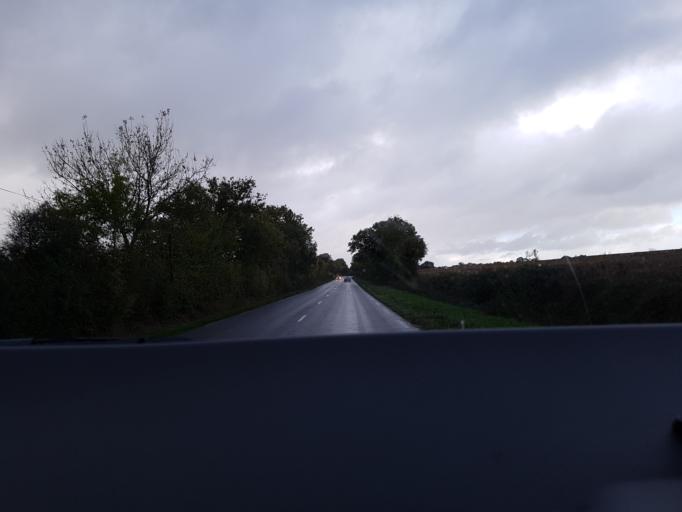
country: FR
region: Poitou-Charentes
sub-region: Departement des Deux-Sevres
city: Melle
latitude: 46.2010
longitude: -0.1613
